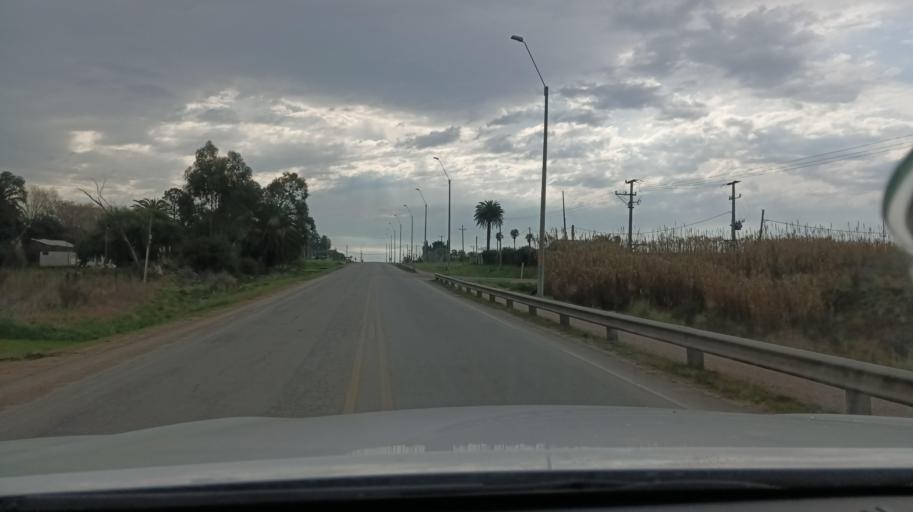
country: UY
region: Canelones
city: Toledo
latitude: -34.7501
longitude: -56.1093
